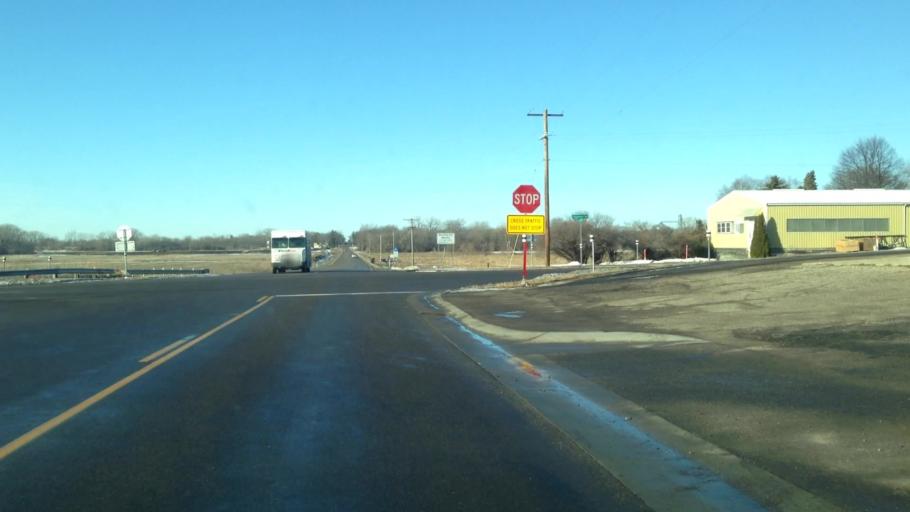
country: US
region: Minnesota
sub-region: Rice County
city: Northfield
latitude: 44.5437
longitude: -93.1362
